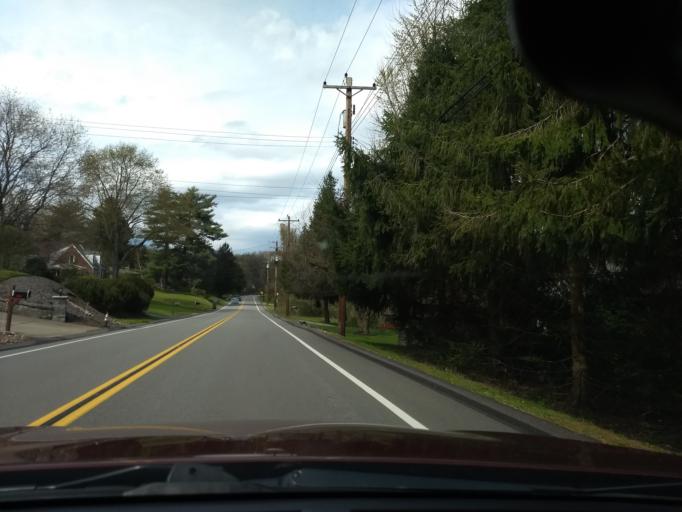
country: US
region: Pennsylvania
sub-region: Allegheny County
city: Allison Park
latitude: 40.5684
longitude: -79.9973
